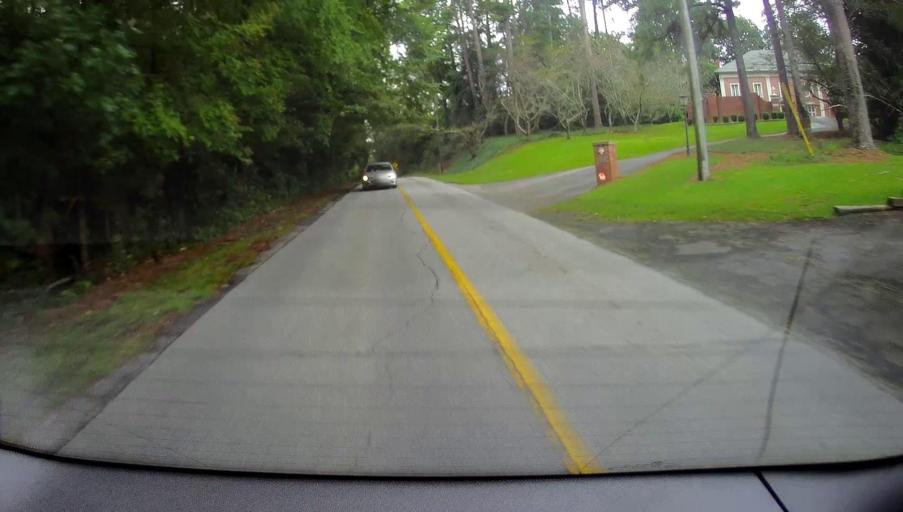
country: US
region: Georgia
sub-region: Bibb County
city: Macon
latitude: 32.8545
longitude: -83.6660
